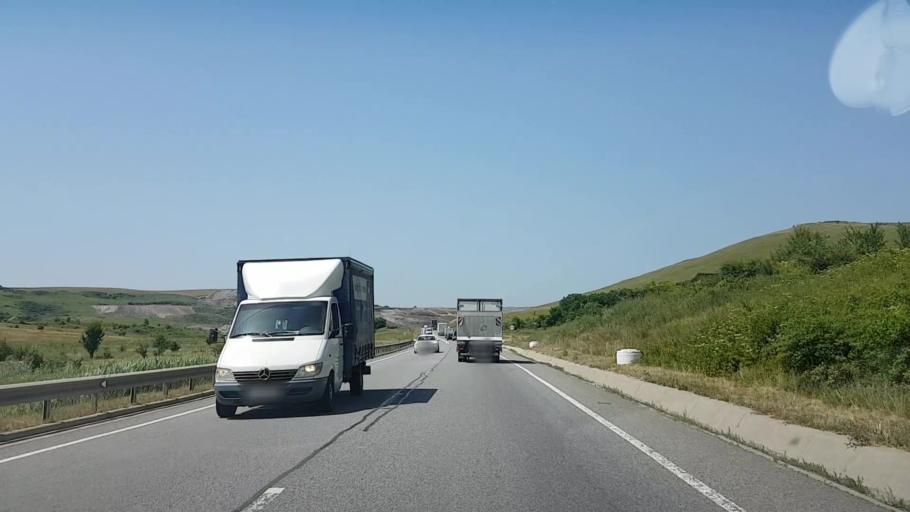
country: RO
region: Cluj
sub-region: Comuna Apahida
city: Dezmir
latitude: 46.7567
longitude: 23.6990
